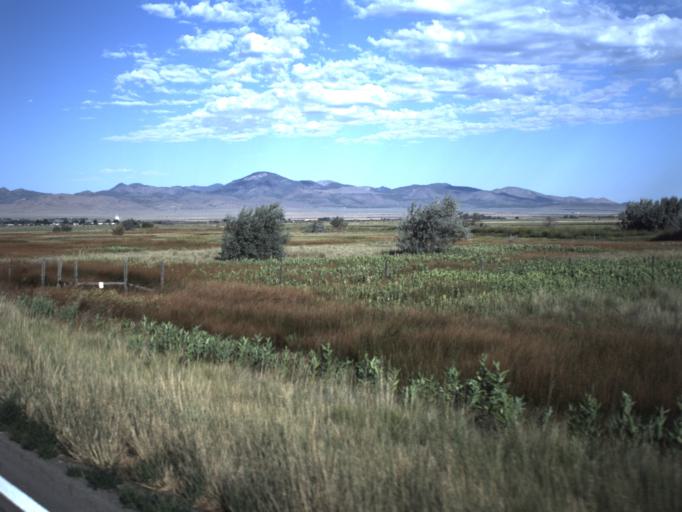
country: US
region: Utah
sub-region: Utah County
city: Genola
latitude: 39.9591
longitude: -111.8715
